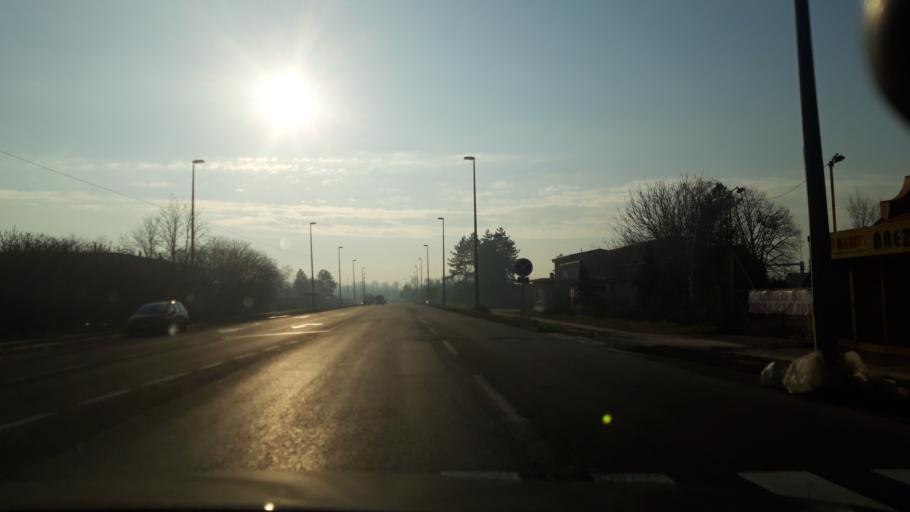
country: RS
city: Pocerski Pricinovic
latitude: 44.7440
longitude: 19.7207
